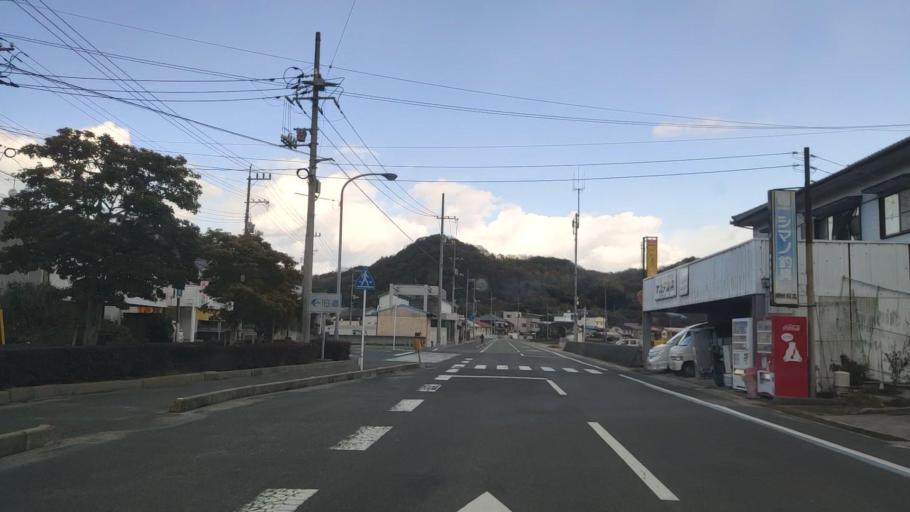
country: JP
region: Hiroshima
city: Innoshima
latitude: 34.2033
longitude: 133.0933
